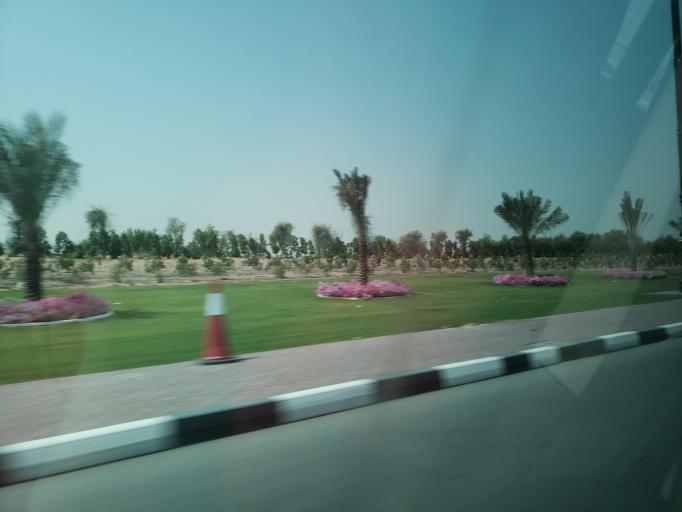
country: AE
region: Ash Shariqah
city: Sharjah
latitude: 25.3071
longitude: 55.5748
